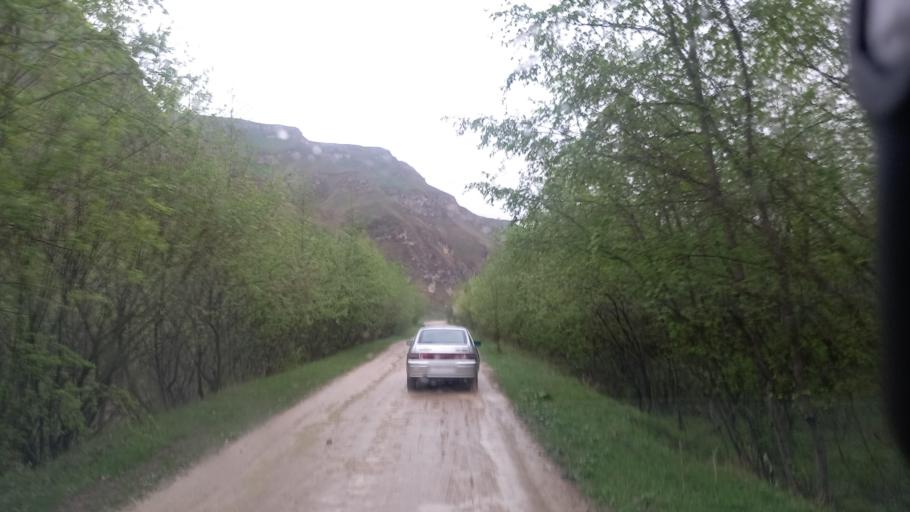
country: RU
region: Kabardino-Balkariya
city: Gundelen
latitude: 43.5978
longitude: 43.0529
